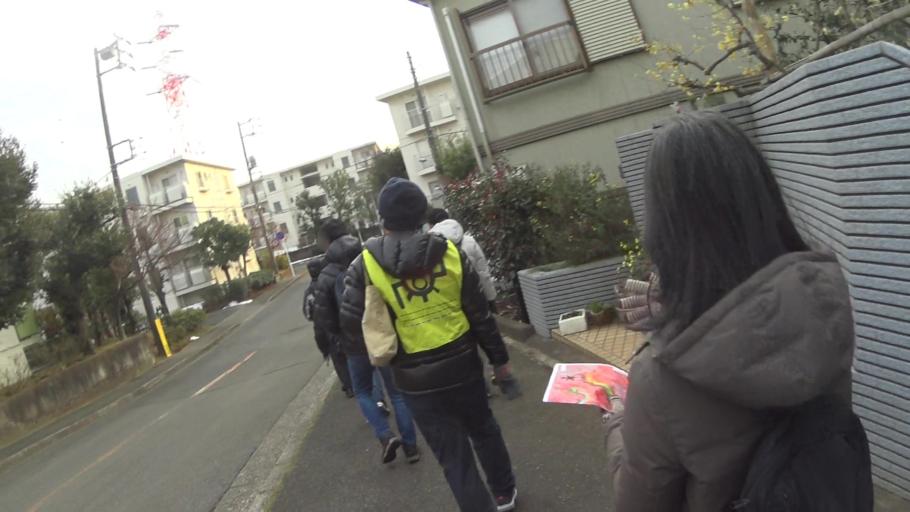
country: JP
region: Chiba
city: Funabashi
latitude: 35.7441
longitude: 140.0079
